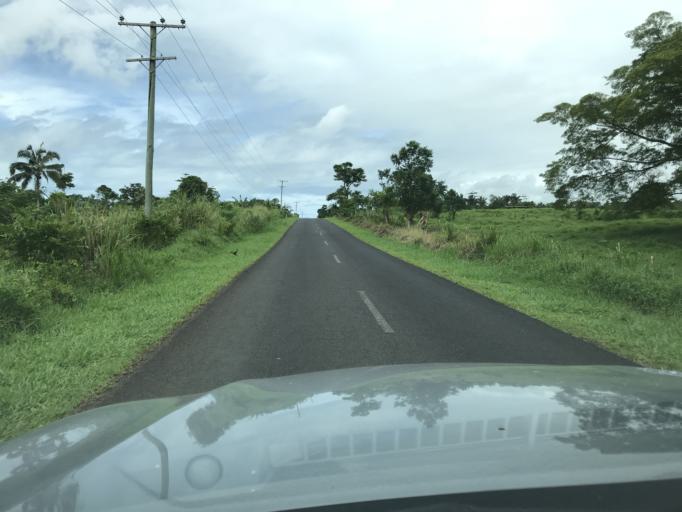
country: WS
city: Nofoali`i
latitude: -13.8758
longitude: -171.9327
